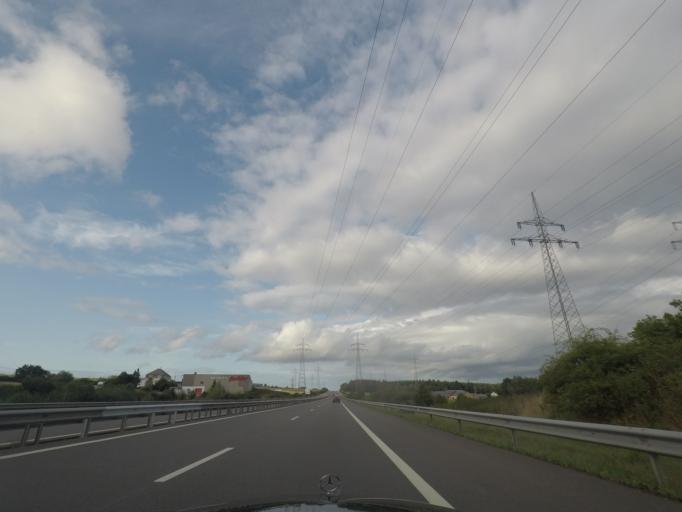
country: LU
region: Luxembourg
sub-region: Canton de Mersch
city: Bissen
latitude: 49.7797
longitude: 6.0898
